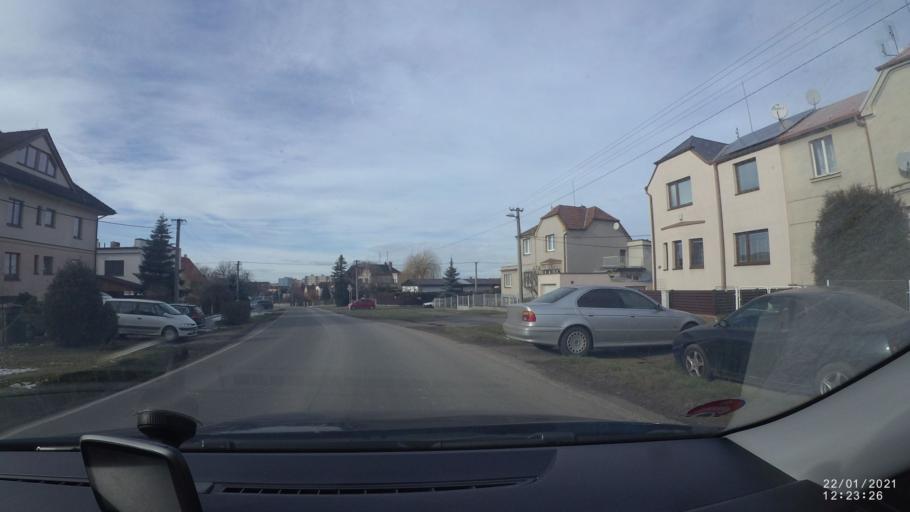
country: CZ
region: Plzensky
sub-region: Okres Plzen-Mesto
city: Pilsen
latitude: 49.7574
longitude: 13.4315
